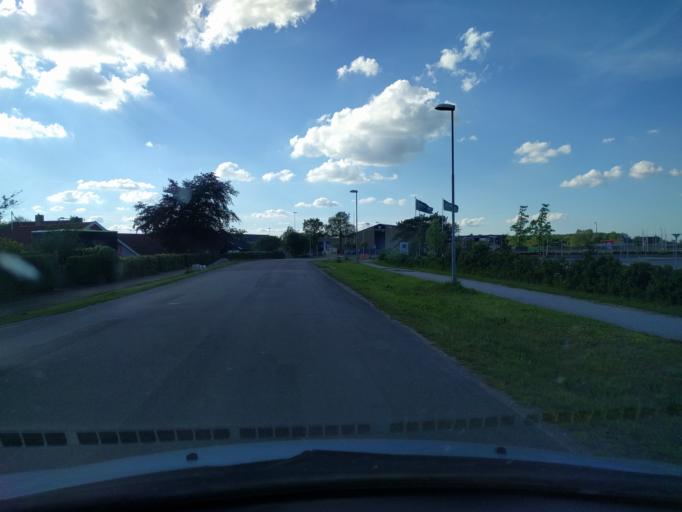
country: DK
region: South Denmark
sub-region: Nyborg Kommune
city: Nyborg
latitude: 55.3086
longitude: 10.8164
